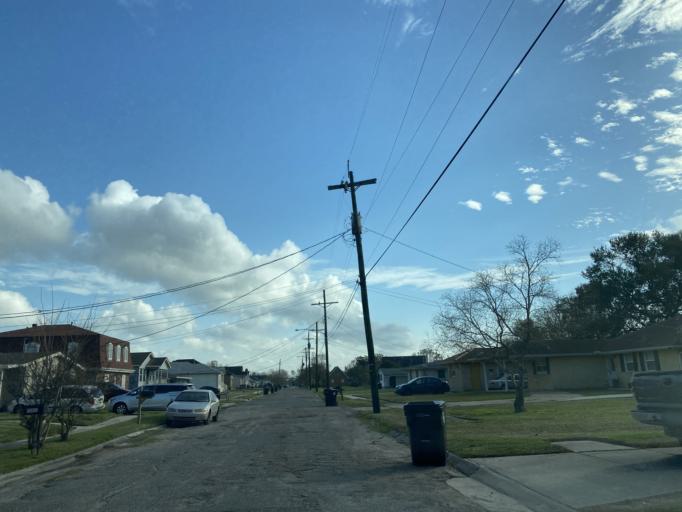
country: US
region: Louisiana
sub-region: Saint Bernard Parish
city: Arabi
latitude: 30.0284
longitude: -90.0376
